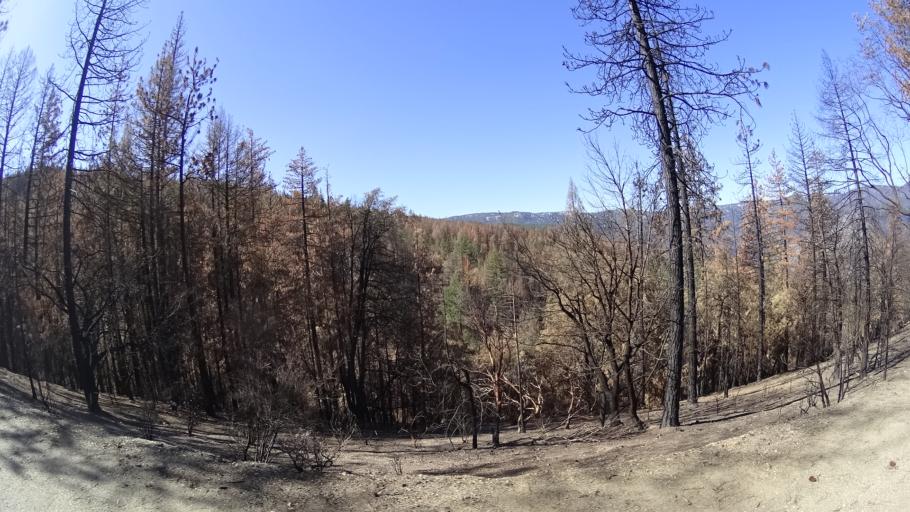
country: US
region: California
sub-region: Tehama County
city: Rancho Tehama Reserve
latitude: 39.6684
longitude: -122.7090
